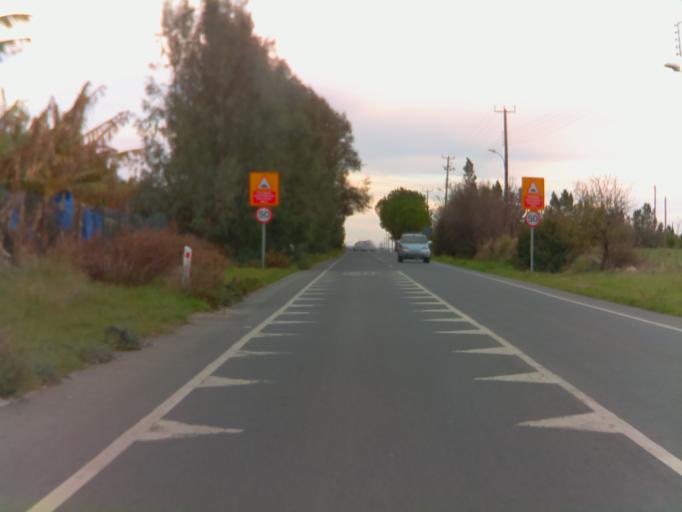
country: CY
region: Pafos
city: Pegeia
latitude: 34.8633
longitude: 32.3707
